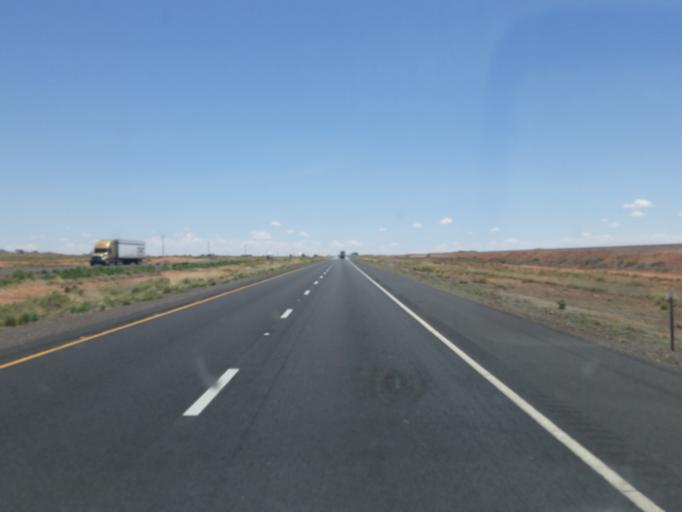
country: US
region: Arizona
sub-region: Coconino County
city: LeChee
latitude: 35.0487
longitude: -110.7721
